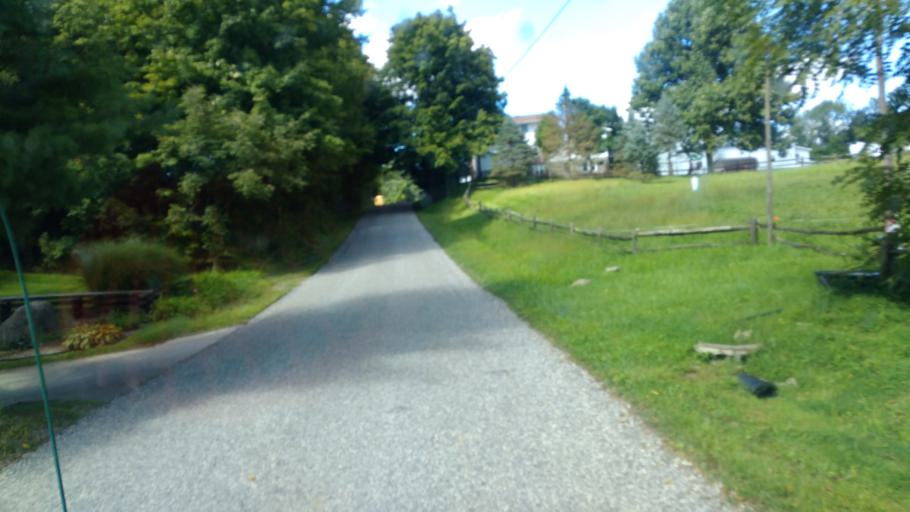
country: US
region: Ohio
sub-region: Holmes County
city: Millersburg
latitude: 40.6295
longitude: -81.8516
